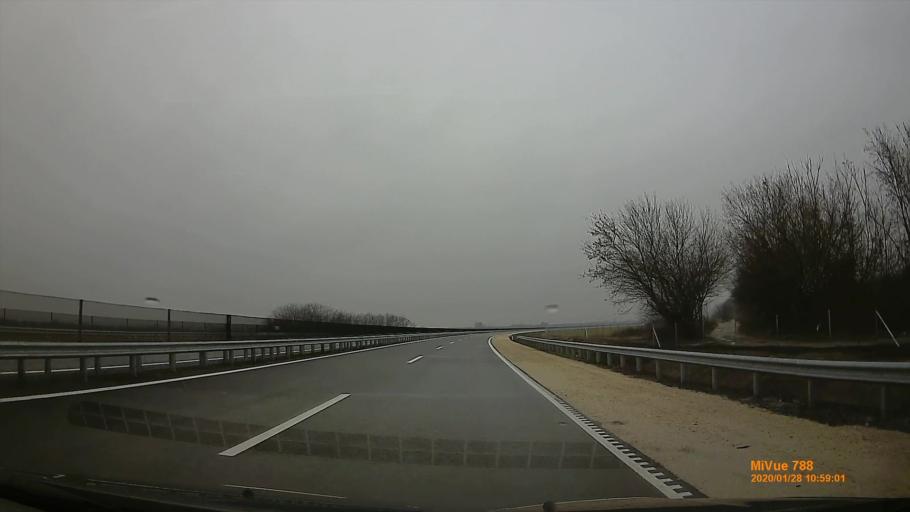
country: HU
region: Pest
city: Peteri
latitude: 47.3794
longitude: 19.3898
